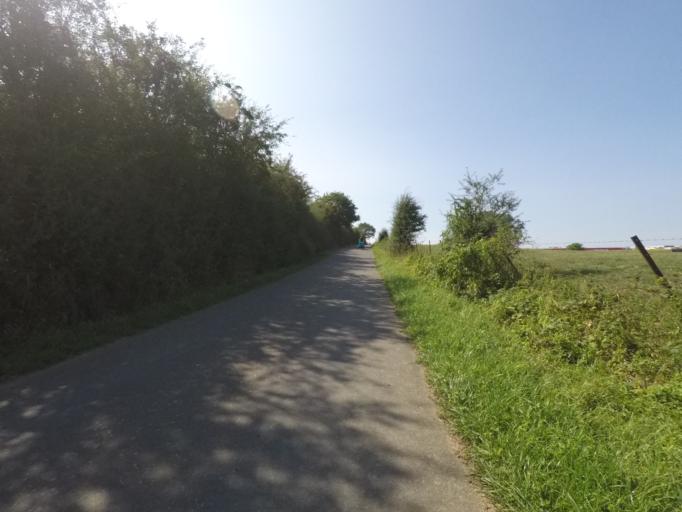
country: LU
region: Luxembourg
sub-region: Canton de Capellen
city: Mamer
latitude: 49.6449
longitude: 6.0197
